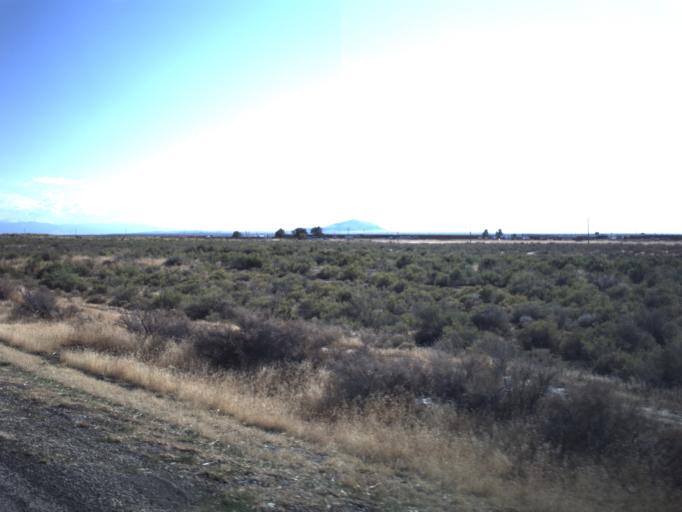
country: US
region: Utah
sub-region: Millard County
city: Delta
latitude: 39.3186
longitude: -112.4809
